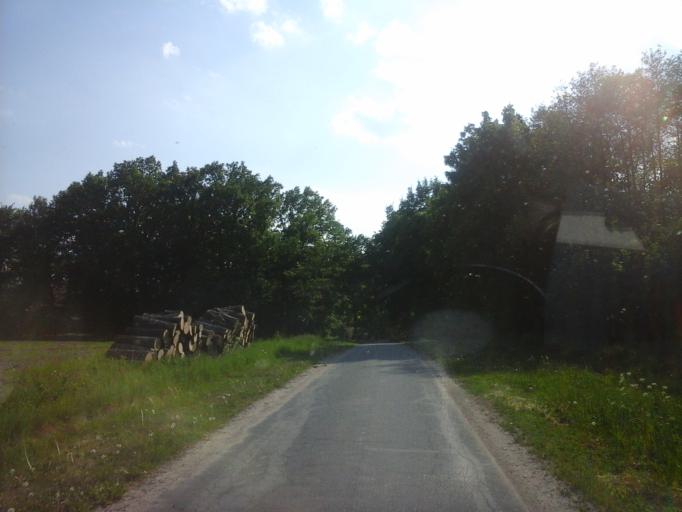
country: PL
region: West Pomeranian Voivodeship
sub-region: Powiat choszczenski
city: Choszczno
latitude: 53.0894
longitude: 15.3945
